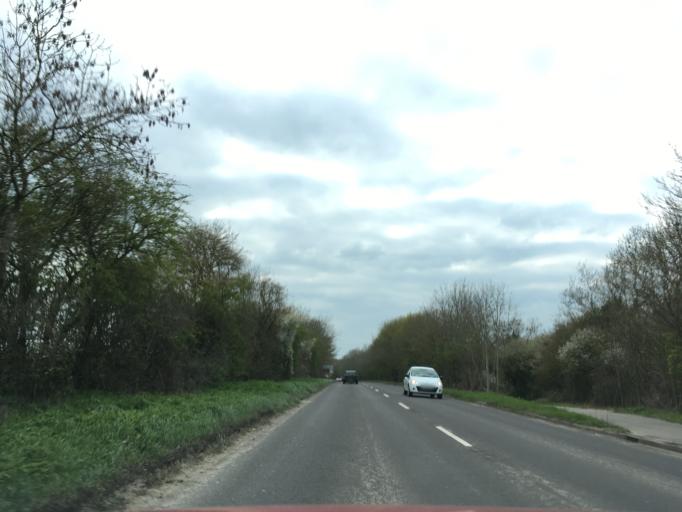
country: GB
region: England
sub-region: Oxfordshire
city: Witney
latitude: 51.7946
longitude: -1.5281
